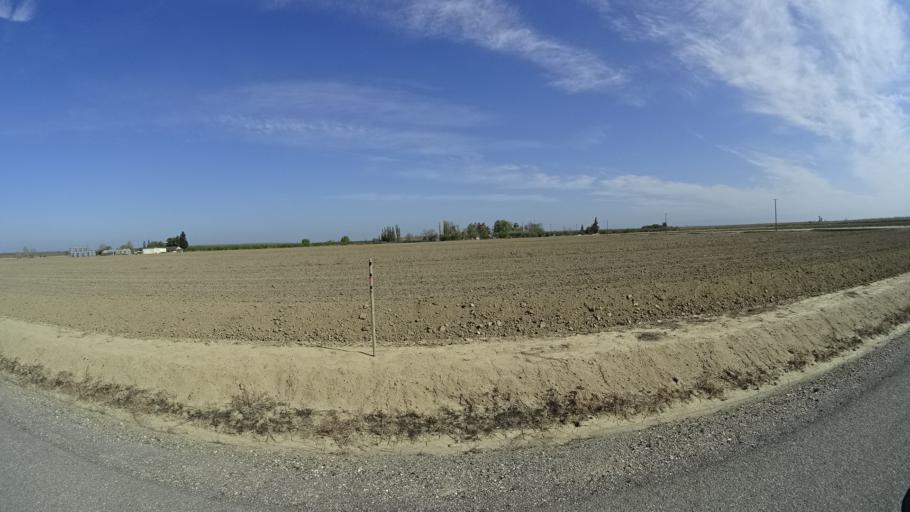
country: US
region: California
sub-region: Glenn County
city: Hamilton City
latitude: 39.6231
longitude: -122.0381
